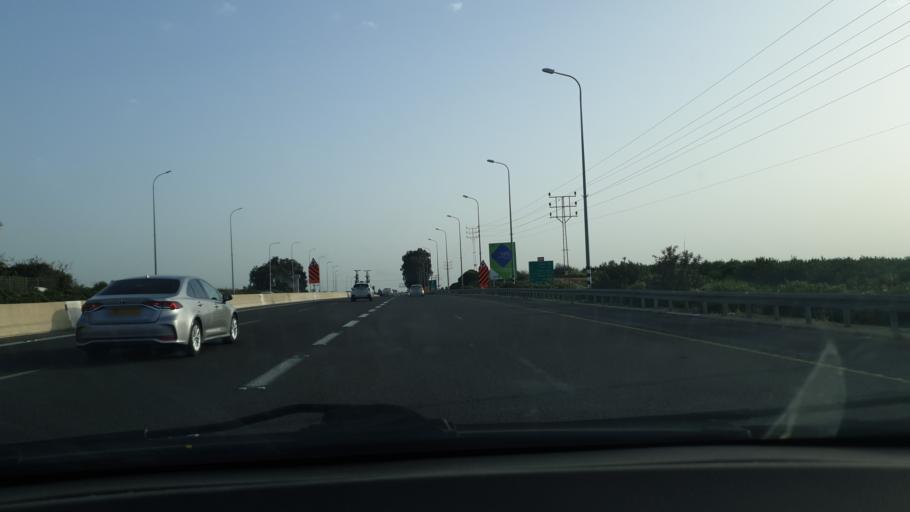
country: IL
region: Central District
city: Even Yehuda
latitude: 32.2501
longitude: 34.8895
